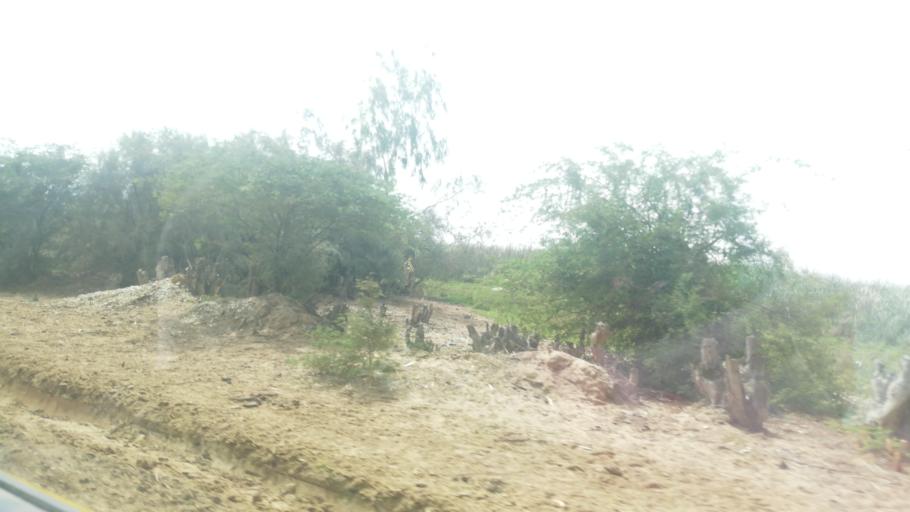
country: SN
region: Saint-Louis
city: Saint-Louis
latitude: 16.0571
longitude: -16.3282
